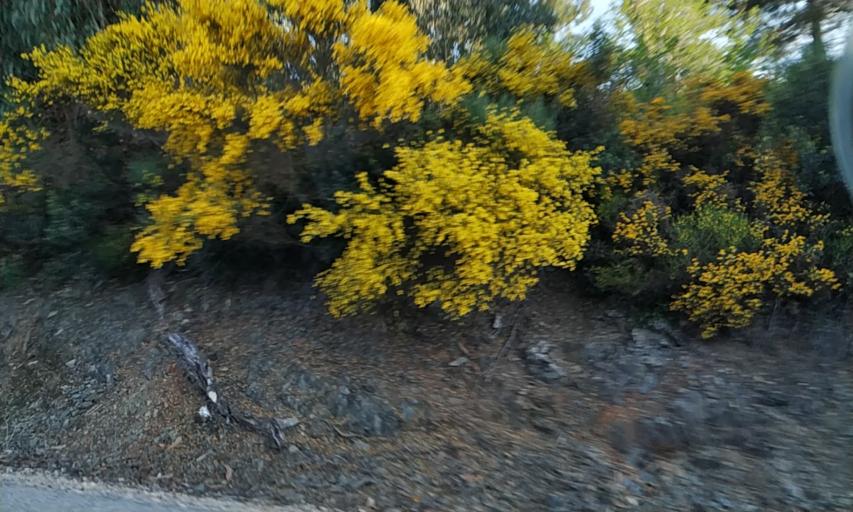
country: PT
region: Portalegre
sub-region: Portalegre
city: Sao Juliao
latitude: 39.3425
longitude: -7.2816
